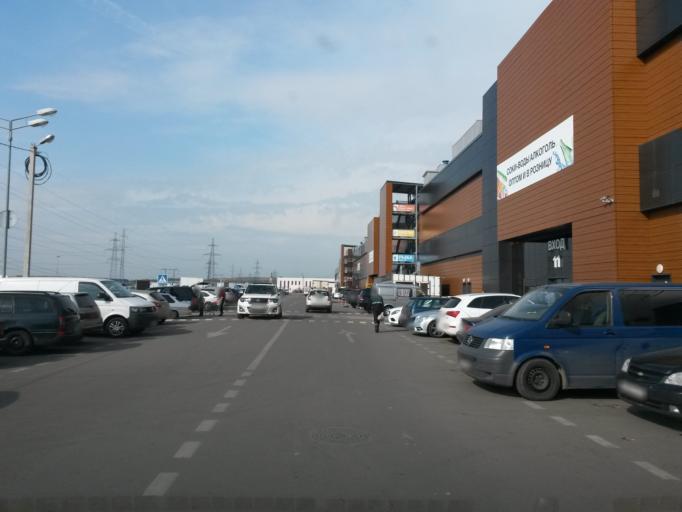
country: RU
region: Moskovskaya
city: Mosrentgen
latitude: 55.5997
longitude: 37.4711
